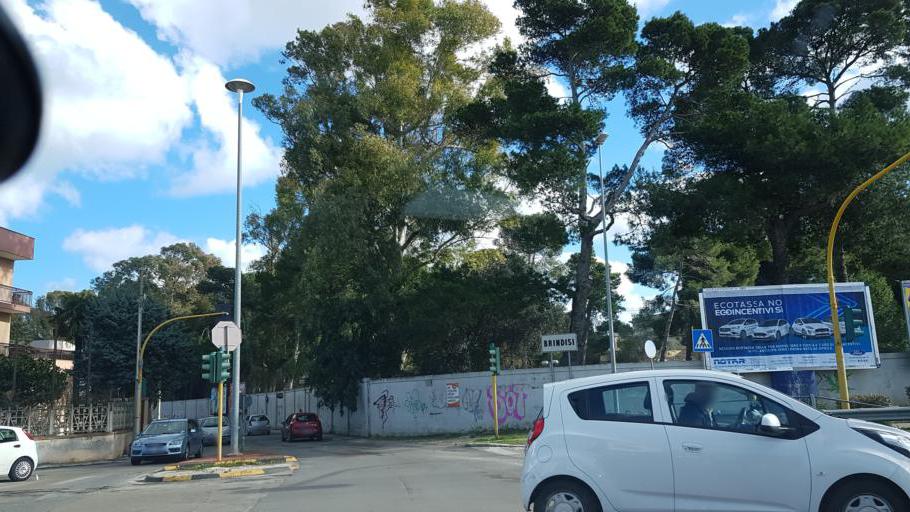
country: IT
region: Apulia
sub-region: Provincia di Brindisi
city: Brindisi
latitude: 40.6282
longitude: 17.9195
